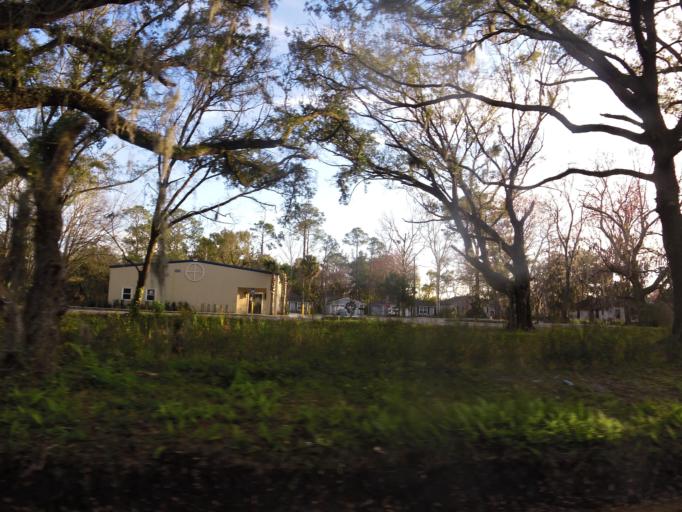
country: US
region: Florida
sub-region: Duval County
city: Jacksonville
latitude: 30.2895
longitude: -81.6428
